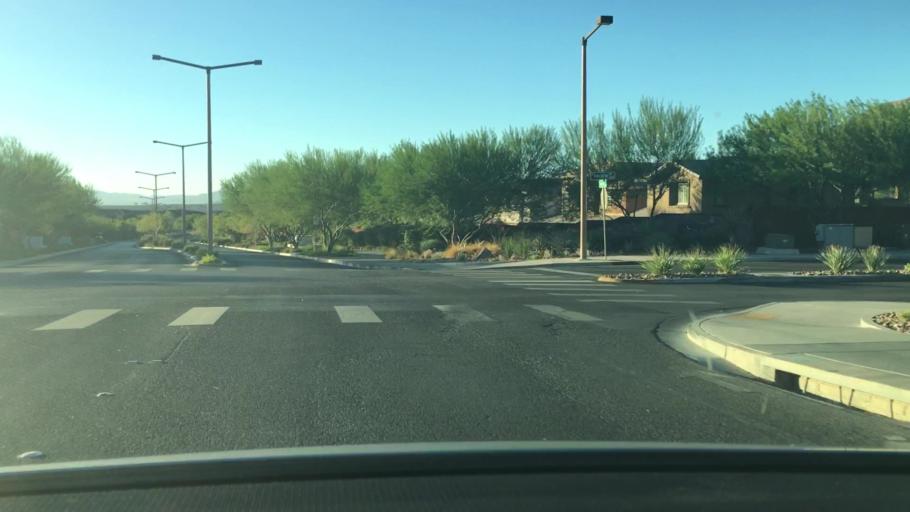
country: US
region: Nevada
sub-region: Clark County
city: Summerlin South
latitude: 36.0881
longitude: -115.3235
